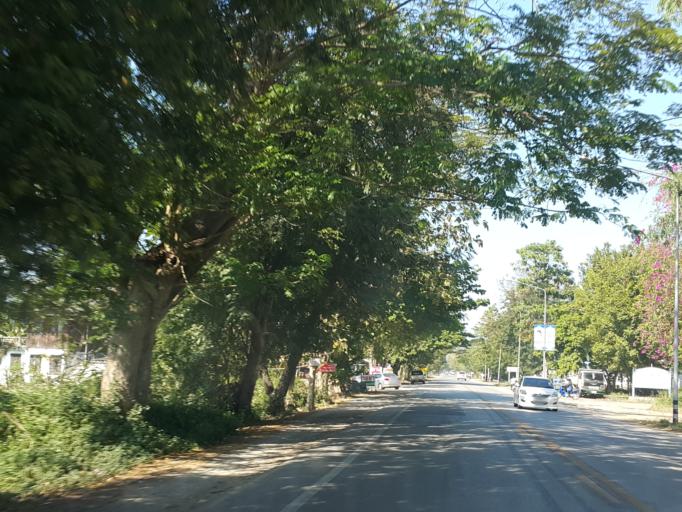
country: TH
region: Chiang Mai
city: Mae Taeng
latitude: 19.0410
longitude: 98.9688
